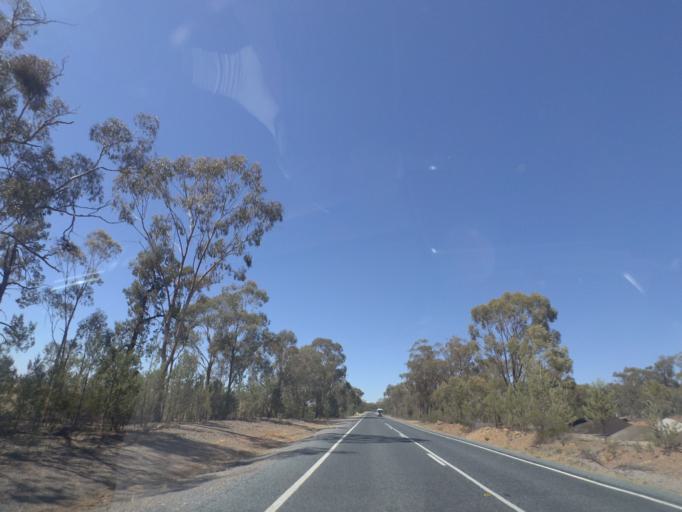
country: AU
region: New South Wales
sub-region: Narrandera
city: Narrandera
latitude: -34.4356
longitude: 146.8423
